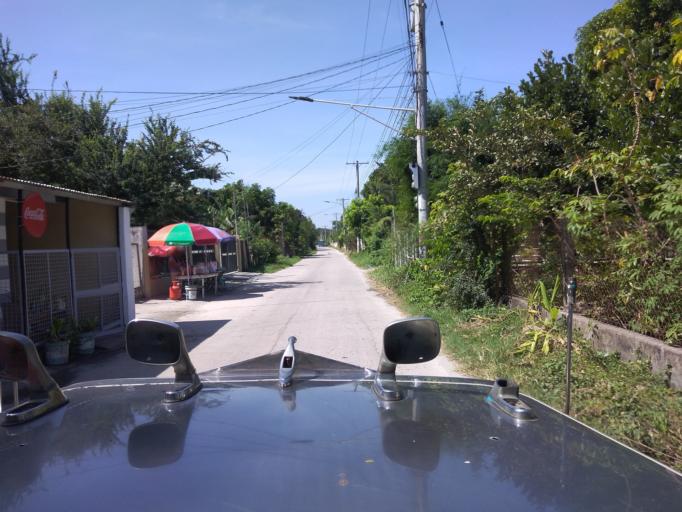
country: PH
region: Central Luzon
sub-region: Province of Pampanga
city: Bacolor
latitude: 15.0073
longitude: 120.6644
